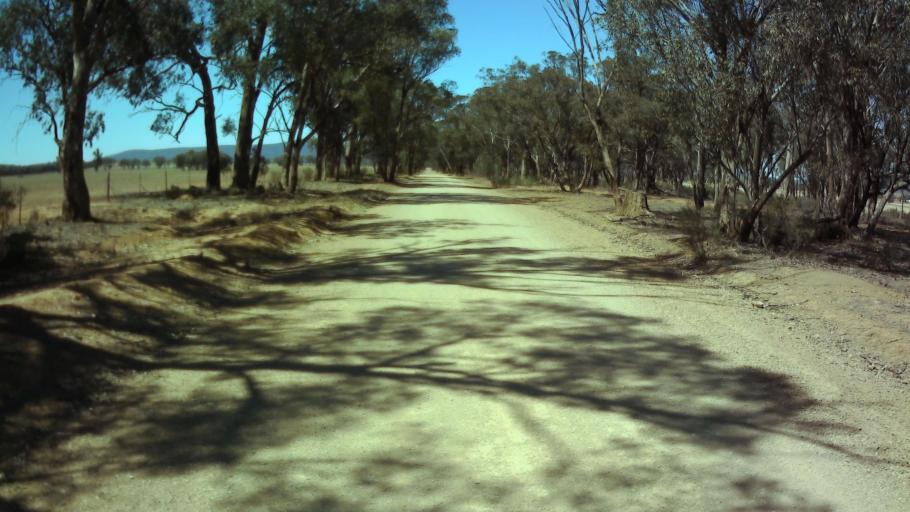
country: AU
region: New South Wales
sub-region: Weddin
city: Grenfell
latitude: -33.8934
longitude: 148.0856
